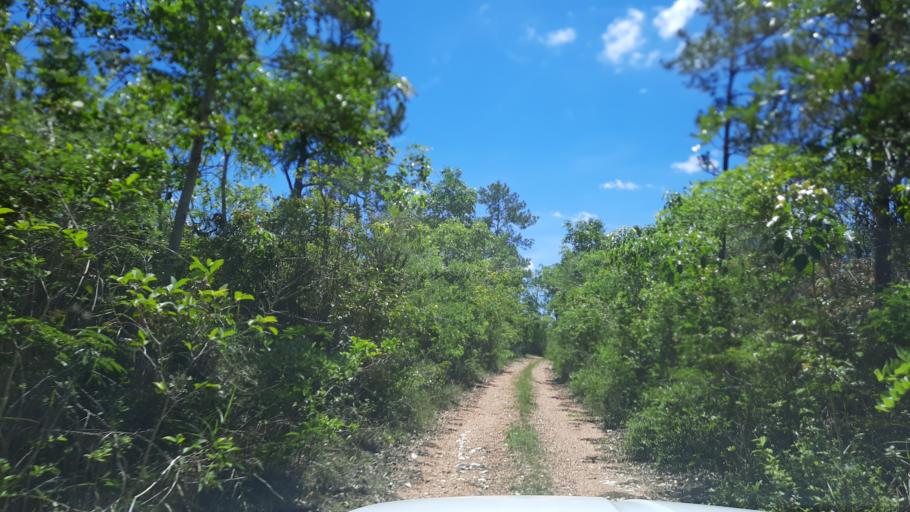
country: BZ
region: Cayo
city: Belmopan
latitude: 17.3579
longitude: -88.5374
